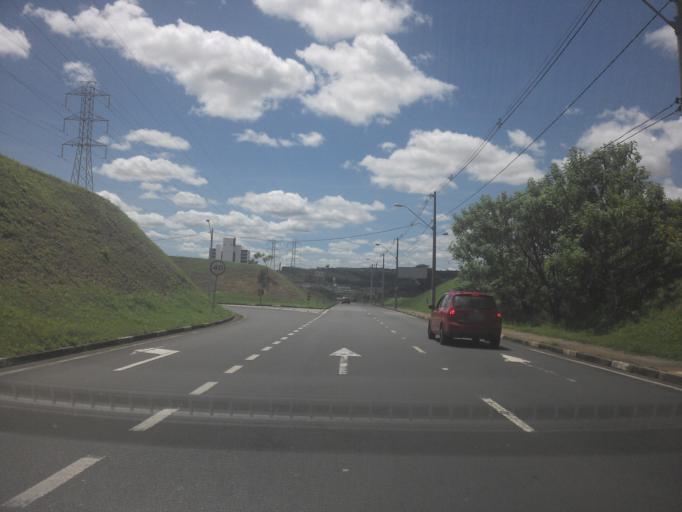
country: BR
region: Sao Paulo
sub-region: Campinas
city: Campinas
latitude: -22.8929
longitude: -47.0224
